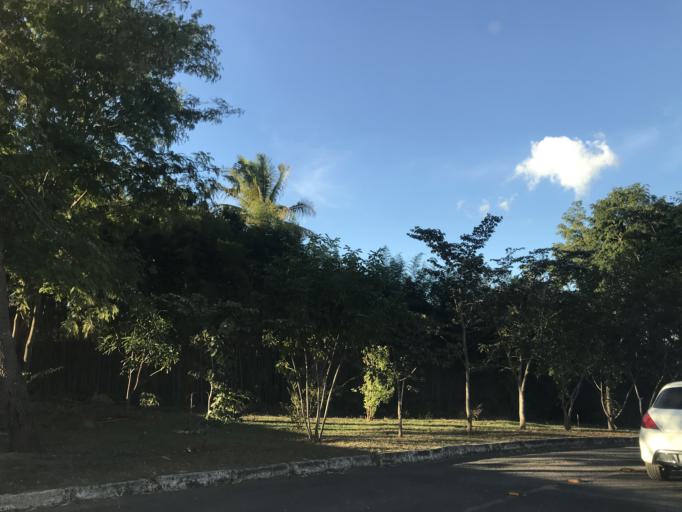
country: BR
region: Federal District
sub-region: Brasilia
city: Brasilia
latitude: -15.8813
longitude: -47.7670
